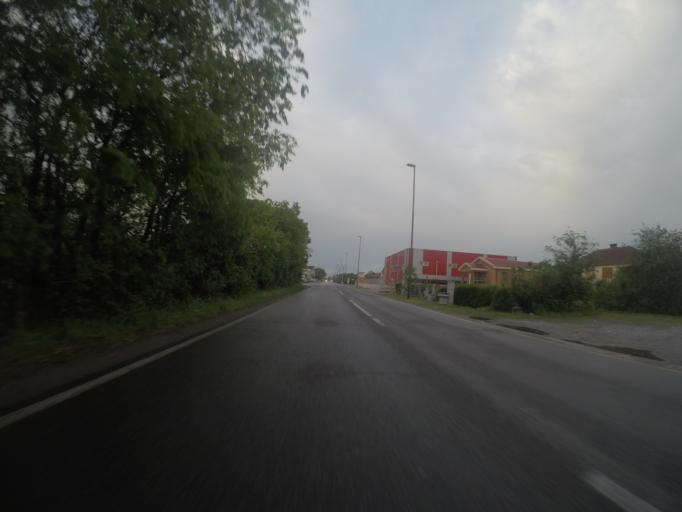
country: ME
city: Mojanovici
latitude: 42.3358
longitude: 19.2211
